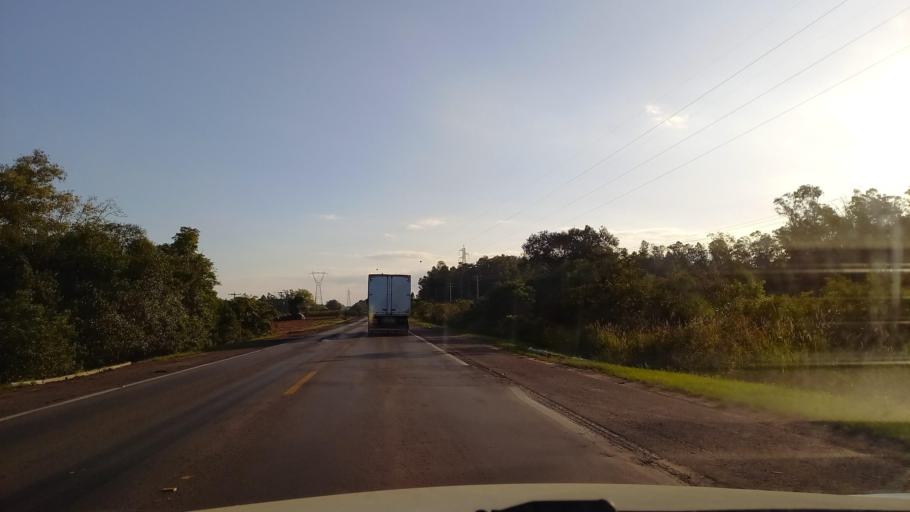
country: BR
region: Rio Grande do Sul
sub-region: Venancio Aires
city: Venancio Aires
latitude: -29.6404
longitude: -52.1658
